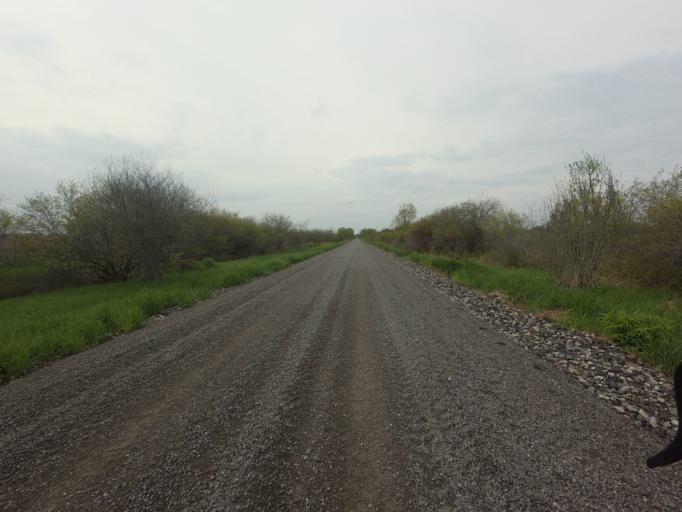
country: CA
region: Ontario
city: Carleton Place
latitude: 45.1957
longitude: -76.1647
